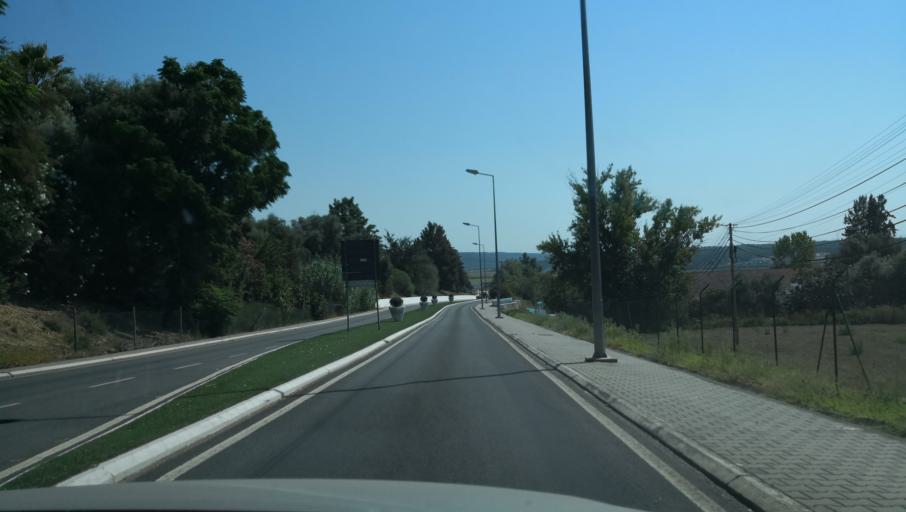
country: PT
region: Setubal
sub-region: Alcacer do Sal
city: Alcacer do Sal
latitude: 38.3751
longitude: -8.5096
